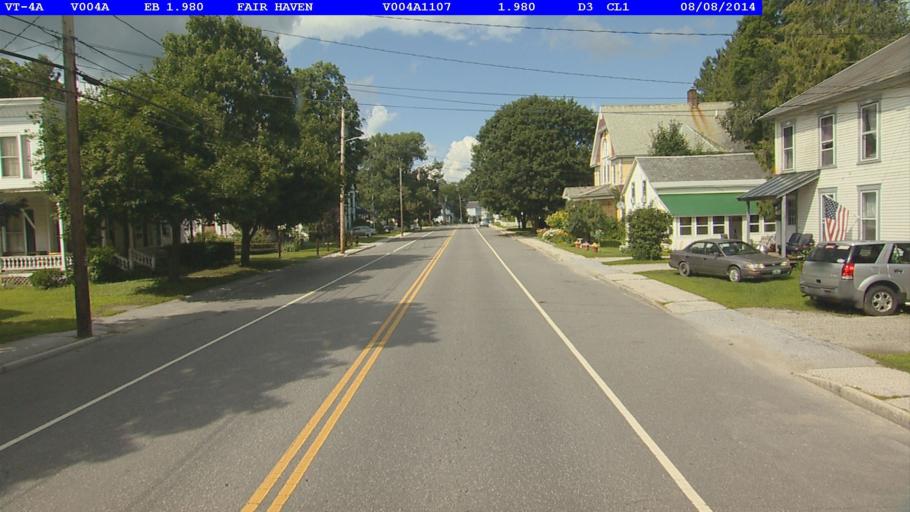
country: US
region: Vermont
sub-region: Rutland County
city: Fair Haven
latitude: 43.5966
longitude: -73.2646
